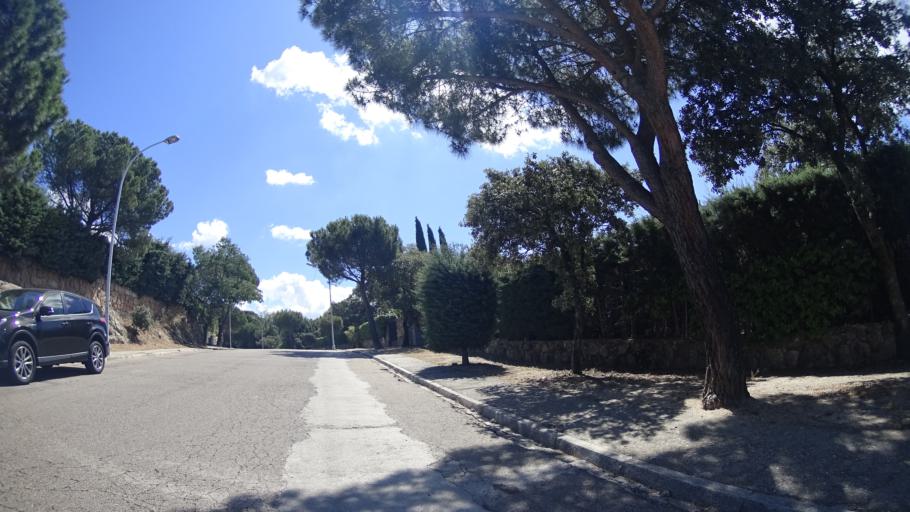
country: ES
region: Madrid
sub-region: Provincia de Madrid
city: Torrelodones
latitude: 40.5852
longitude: -3.9225
